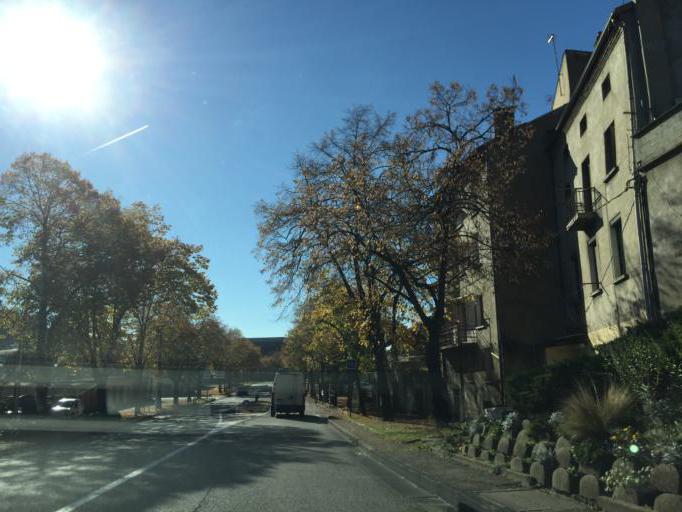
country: FR
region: Rhone-Alpes
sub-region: Departement de la Loire
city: Chateauneuf
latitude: 45.5343
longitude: 4.6317
